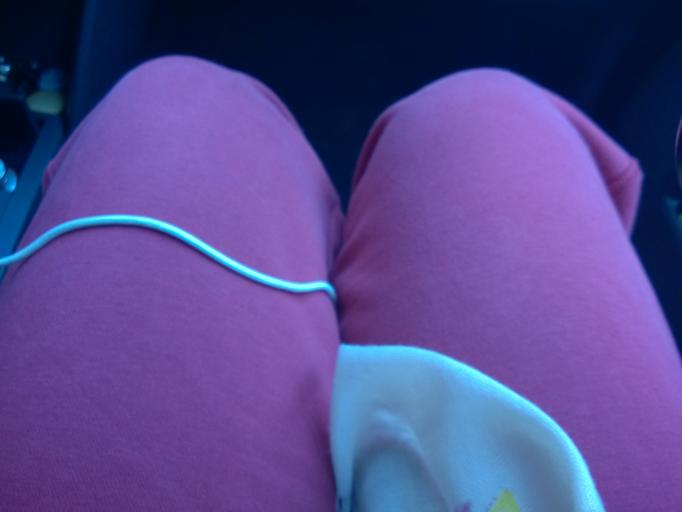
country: GR
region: Attica
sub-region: Nomarchia Athinas
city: Khalandrion
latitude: 38.0152
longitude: 23.8075
